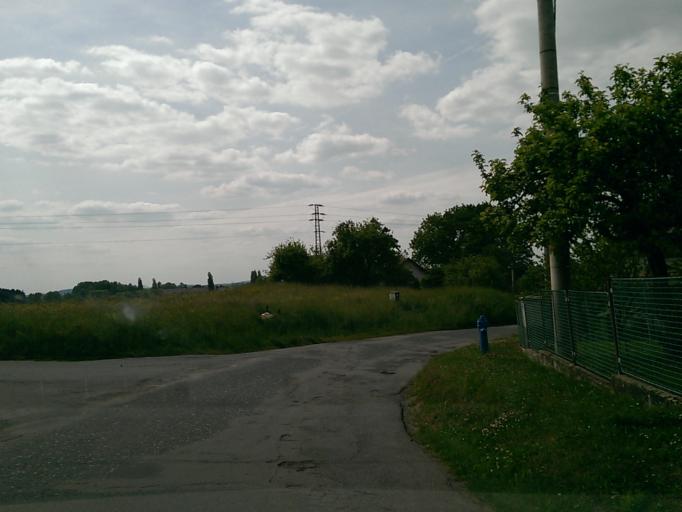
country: CZ
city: Prisovice
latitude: 50.5606
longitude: 15.1015
